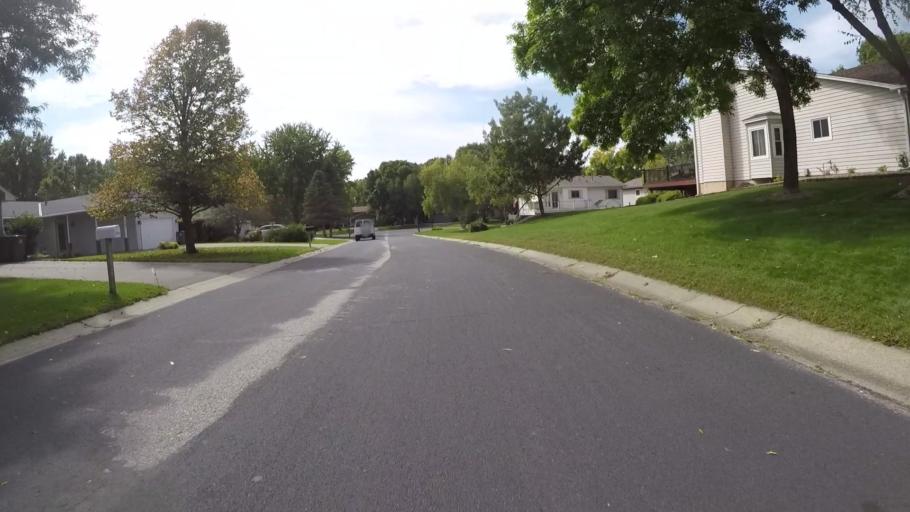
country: US
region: Minnesota
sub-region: Hennepin County
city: Eden Prairie
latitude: 44.8715
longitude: -93.4482
